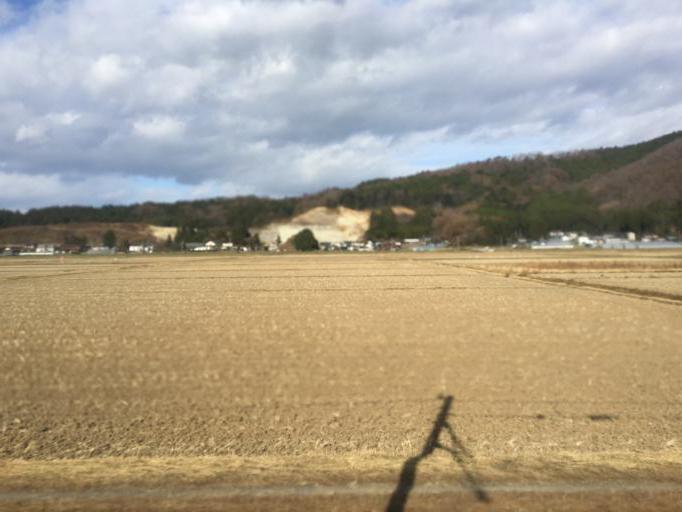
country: JP
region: Miyagi
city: Iwanuma
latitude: 38.0873
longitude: 140.8231
